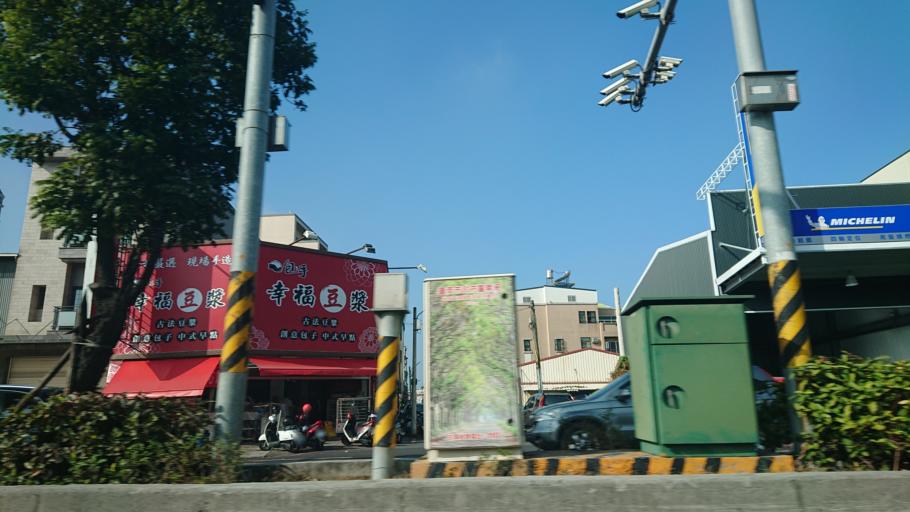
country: TW
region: Taiwan
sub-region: Tainan
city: Tainan
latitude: 23.0079
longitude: 120.1860
